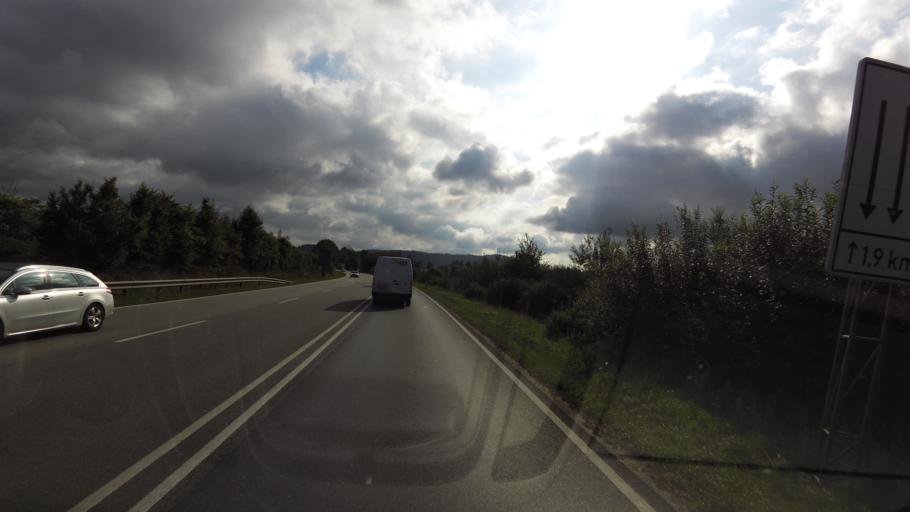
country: DE
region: Bavaria
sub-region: Upper Palatinate
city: Cham
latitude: 49.2003
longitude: 12.6645
